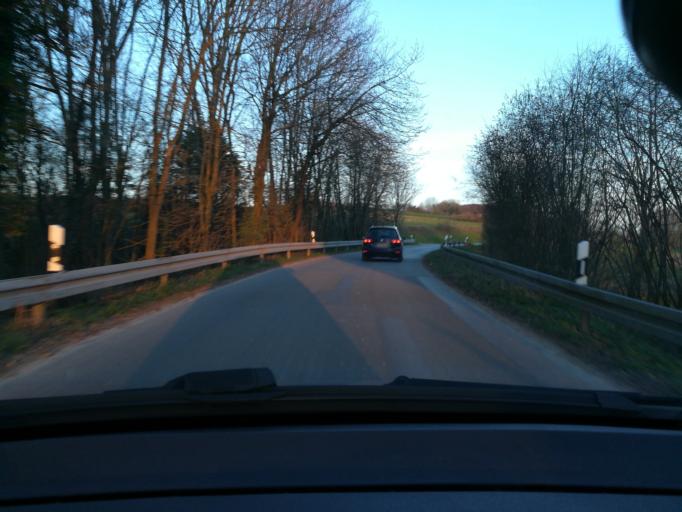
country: DE
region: North Rhine-Westphalia
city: Halle
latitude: 52.0911
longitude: 8.3501
